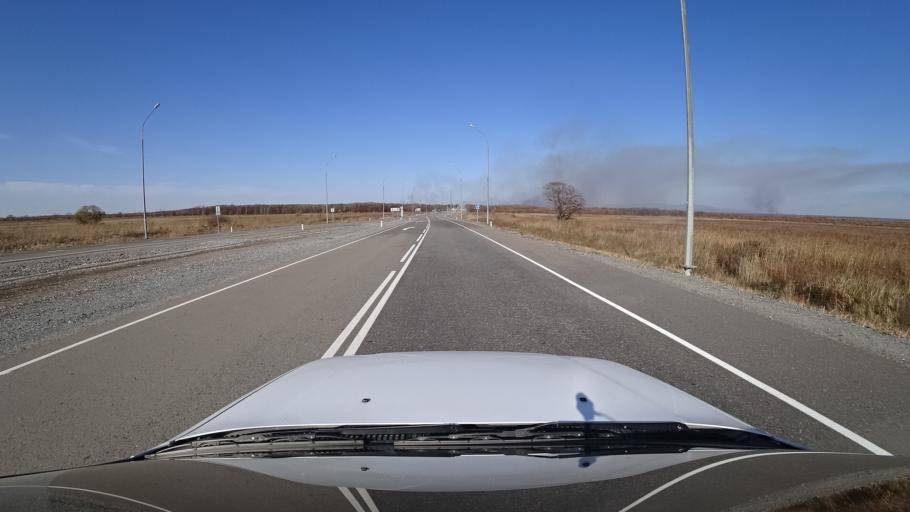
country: RU
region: Primorskiy
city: Dal'nerechensk
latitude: 45.8640
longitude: 133.7204
